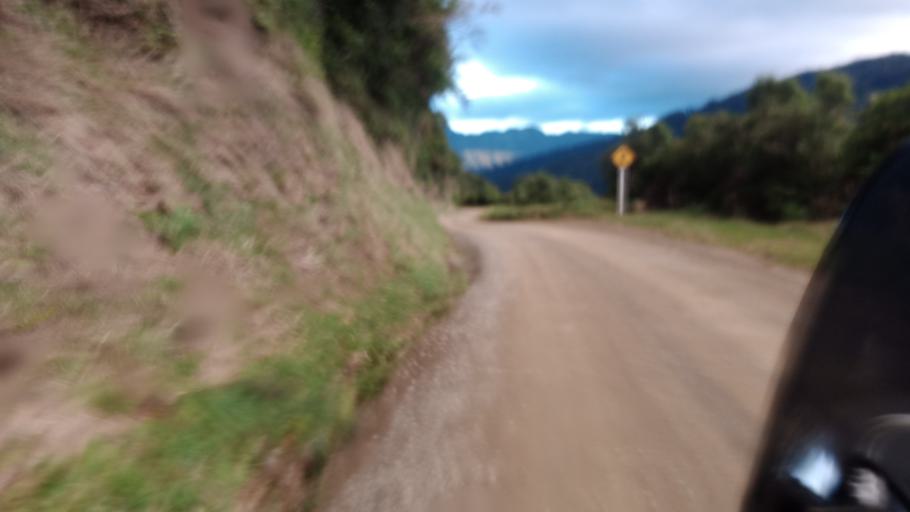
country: NZ
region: Hawke's Bay
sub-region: Wairoa District
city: Wairoa
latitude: -38.7275
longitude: 177.0657
